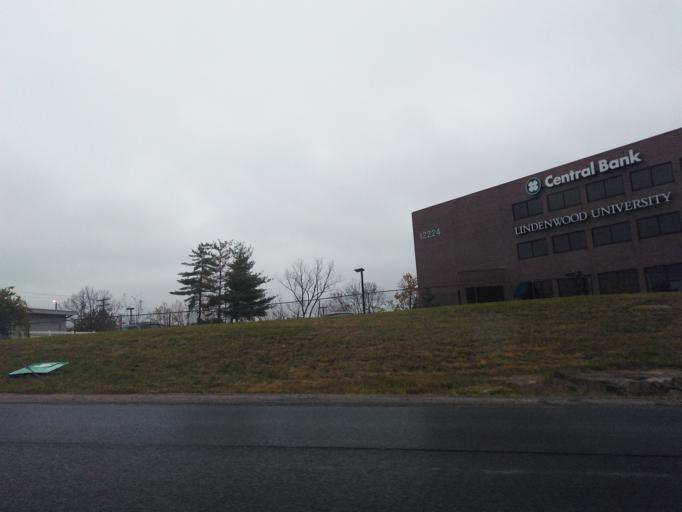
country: US
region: Missouri
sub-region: Saint Louis County
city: Concord
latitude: 38.5129
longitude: -90.3694
